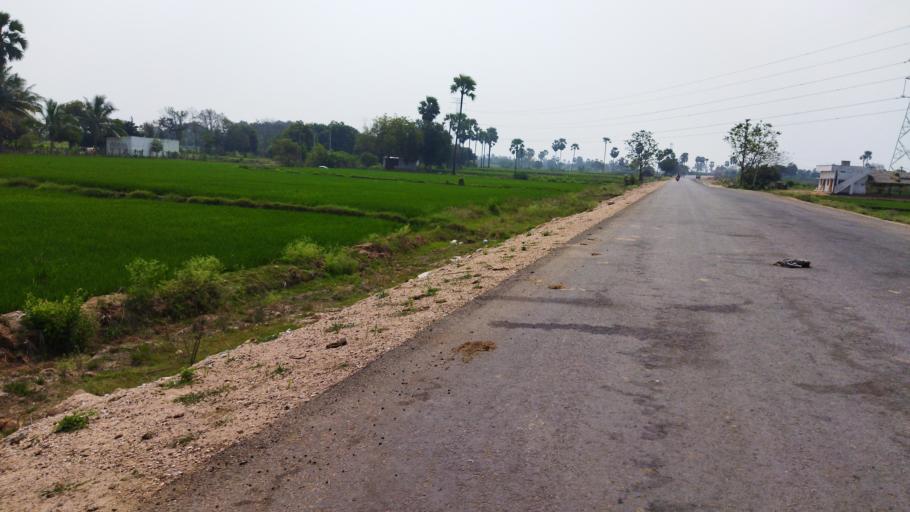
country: IN
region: Telangana
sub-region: Nalgonda
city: Nalgonda
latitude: 17.1162
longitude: 79.3622
